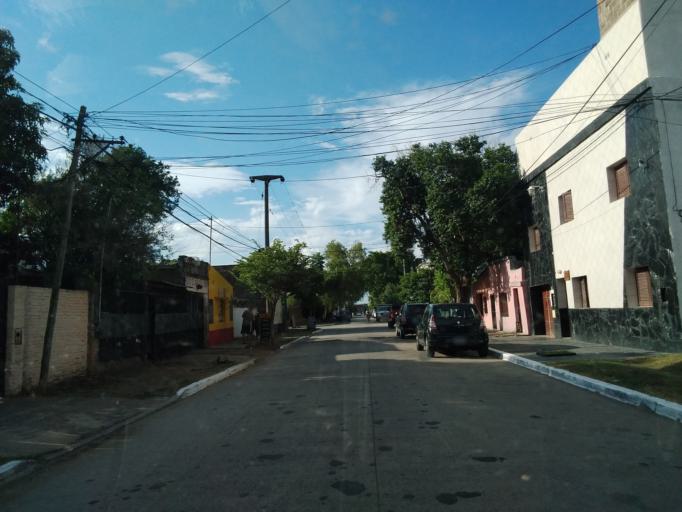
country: AR
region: Corrientes
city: Corrientes
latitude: -27.4649
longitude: -58.8167
